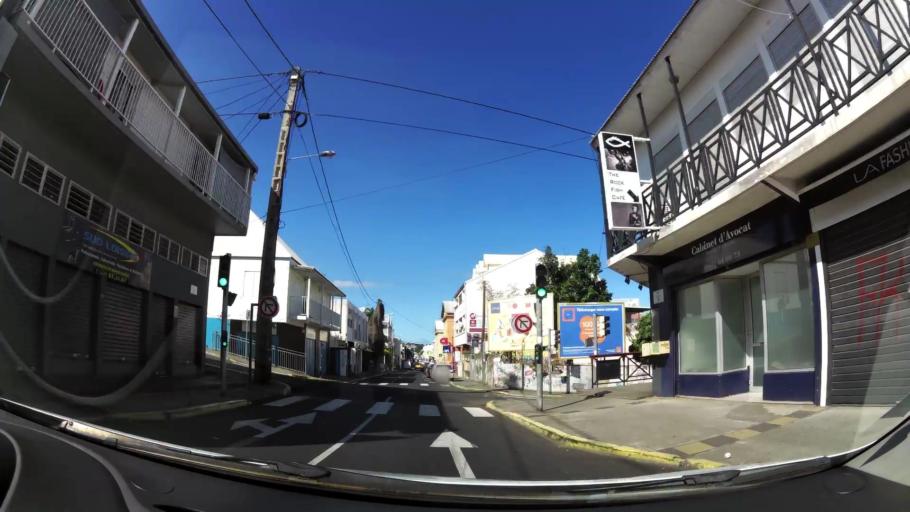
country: RE
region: Reunion
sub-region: Reunion
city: Saint-Pierre
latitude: -21.3374
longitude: 55.4737
